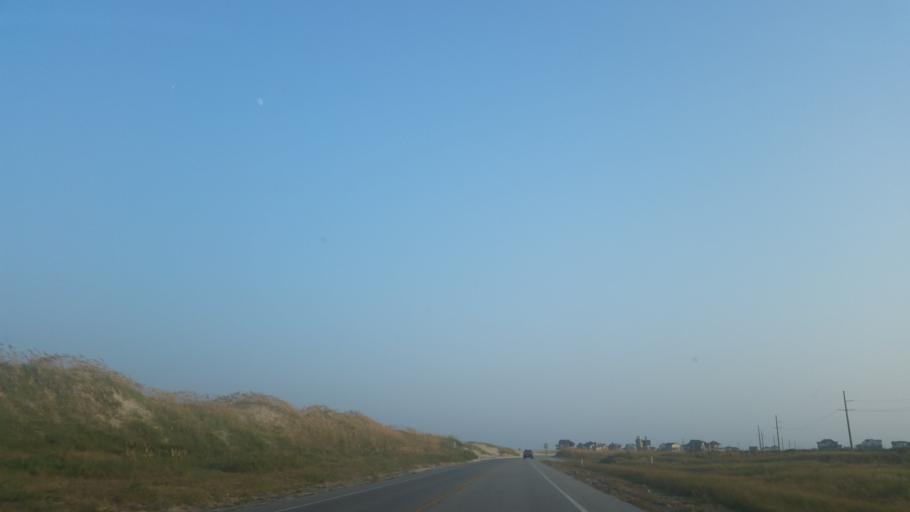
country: US
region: North Carolina
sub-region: Dare County
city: Wanchese
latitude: 35.6130
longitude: -75.4673
